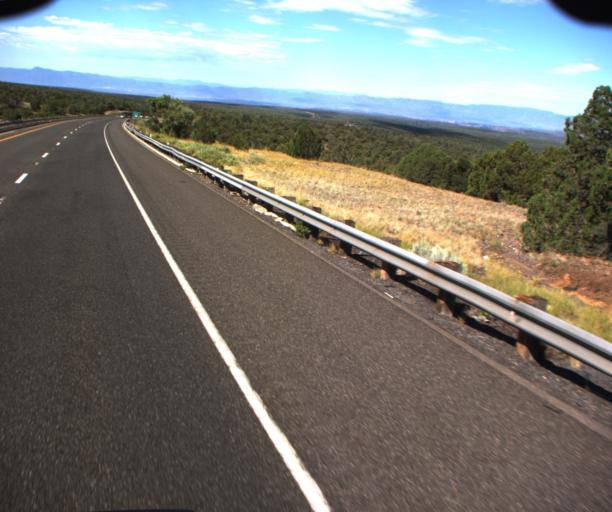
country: US
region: Arizona
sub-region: Yavapai County
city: Village of Oak Creek (Big Park)
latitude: 34.7886
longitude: -111.6047
